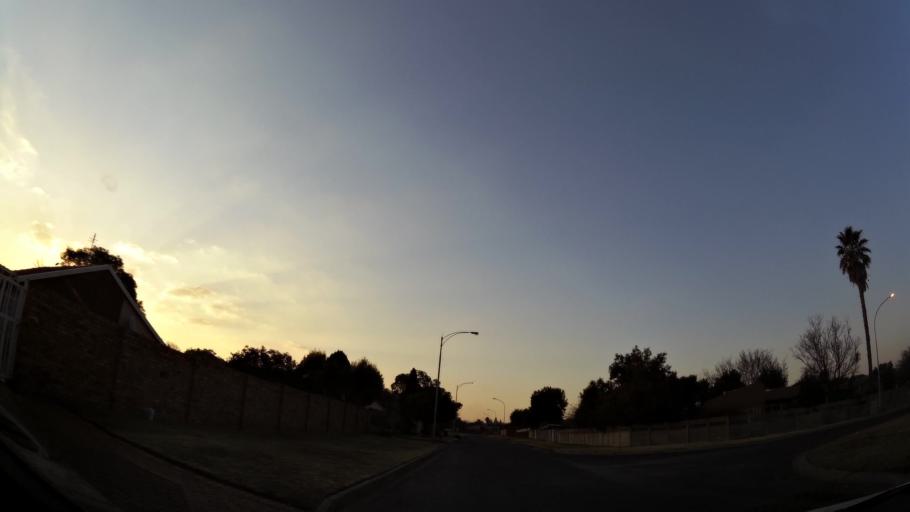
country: ZA
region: Gauteng
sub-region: Ekurhuleni Metropolitan Municipality
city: Springs
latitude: -26.3113
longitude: 28.4531
